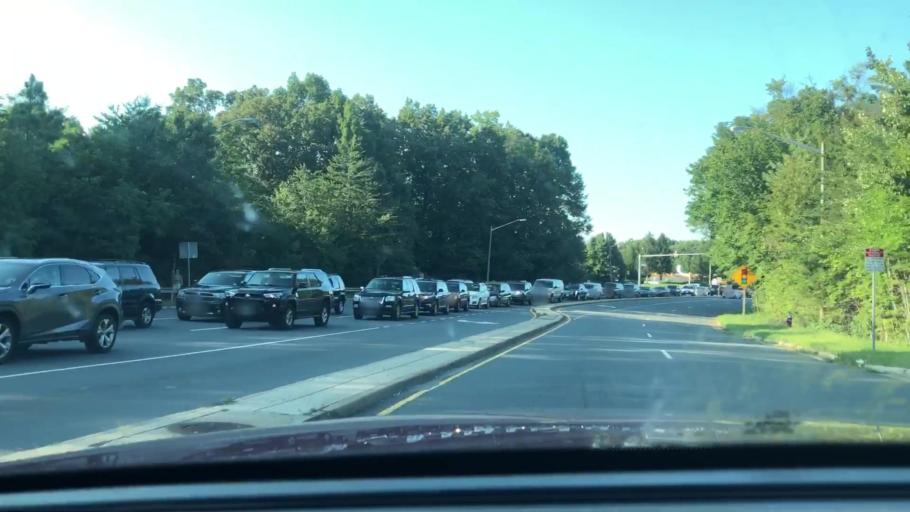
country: US
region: Virginia
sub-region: Fairfax County
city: Centreville
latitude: 38.8309
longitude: -77.4127
